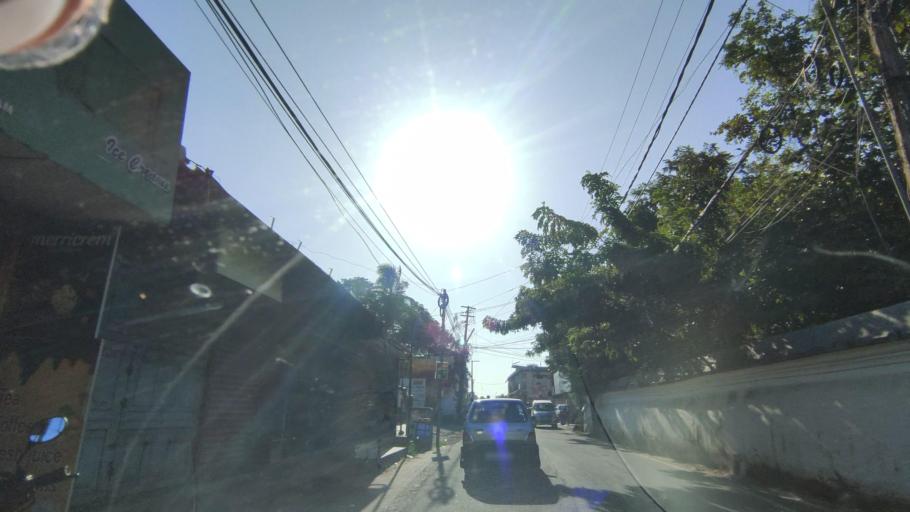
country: IN
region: Kerala
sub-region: Kottayam
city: Kottayam
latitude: 9.5900
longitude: 76.5186
